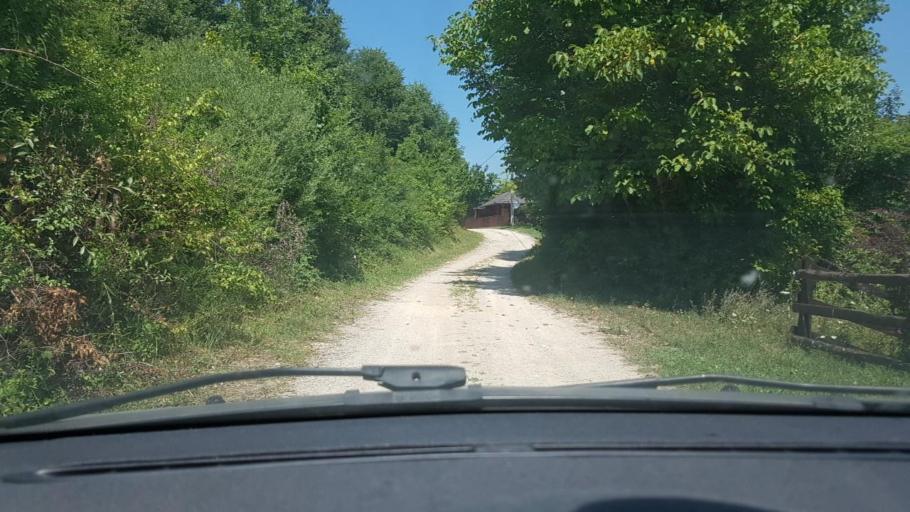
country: BA
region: Federation of Bosnia and Herzegovina
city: Orasac
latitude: 44.5656
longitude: 16.0801
